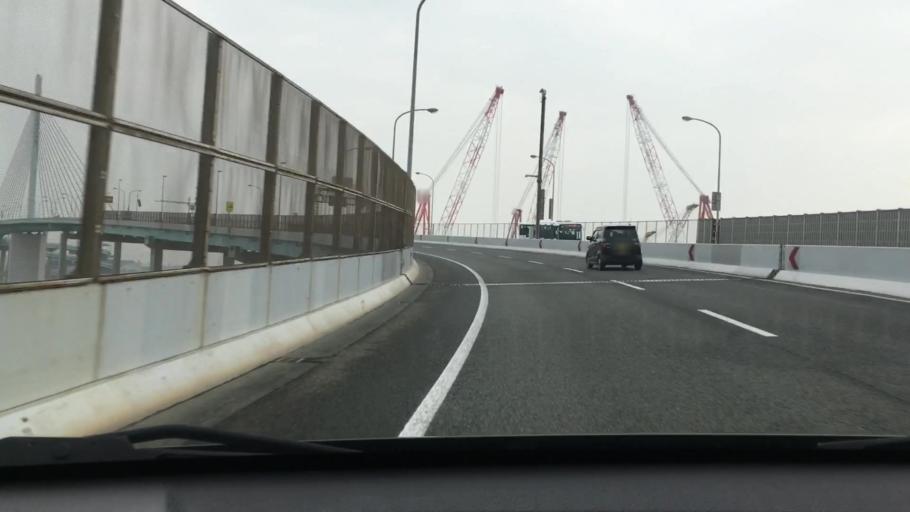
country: JP
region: Fukuoka
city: Fukuoka-shi
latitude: 33.5994
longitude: 130.3788
